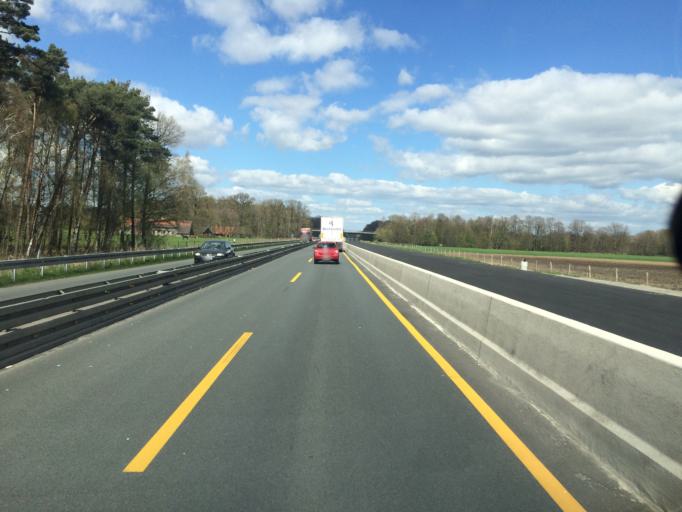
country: DE
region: North Rhine-Westphalia
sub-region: Regierungsbezirk Munster
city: Legden
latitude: 52.0650
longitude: 7.0681
